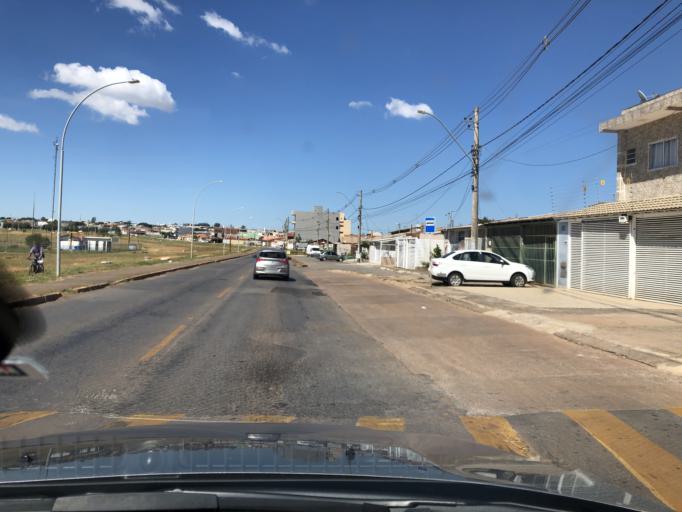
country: BR
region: Federal District
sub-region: Brasilia
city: Brasilia
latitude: -15.8833
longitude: -48.0538
